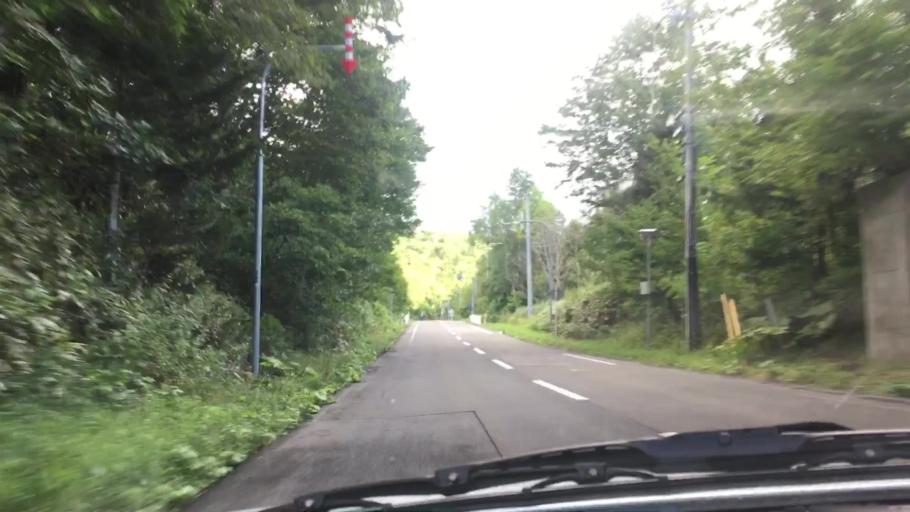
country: JP
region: Hokkaido
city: Shimo-furano
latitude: 43.0996
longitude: 142.6847
